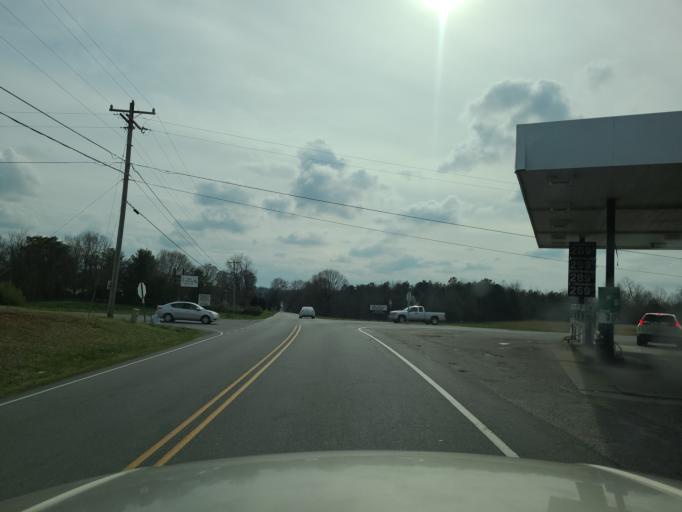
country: US
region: North Carolina
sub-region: Cleveland County
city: Boiling Springs
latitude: 35.2552
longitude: -81.7070
